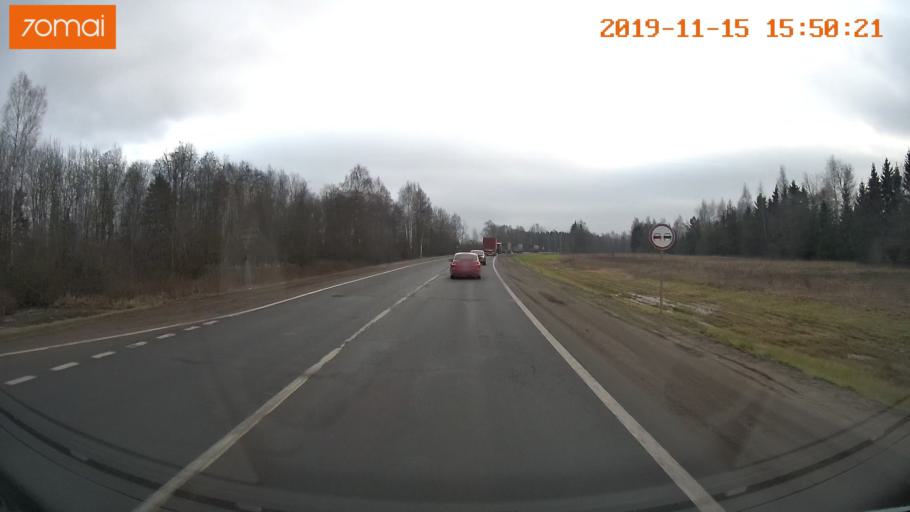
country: RU
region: Jaroslavl
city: Yaroslavl
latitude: 57.9063
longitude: 40.0132
